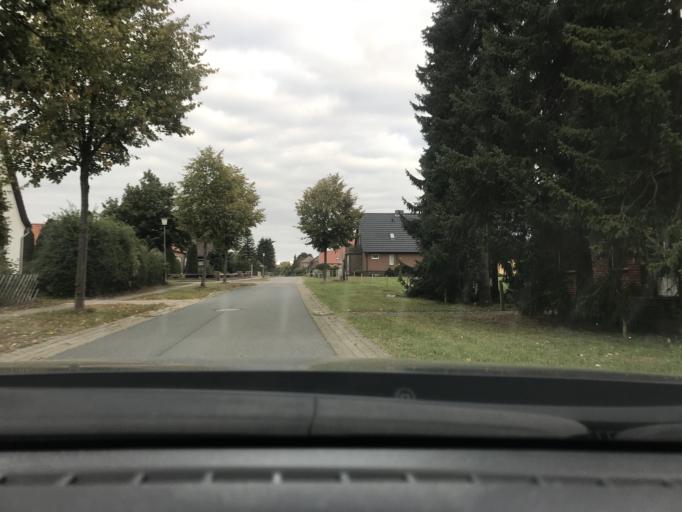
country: DE
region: Lower Saxony
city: Suderburg
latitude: 52.9050
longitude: 10.4259
